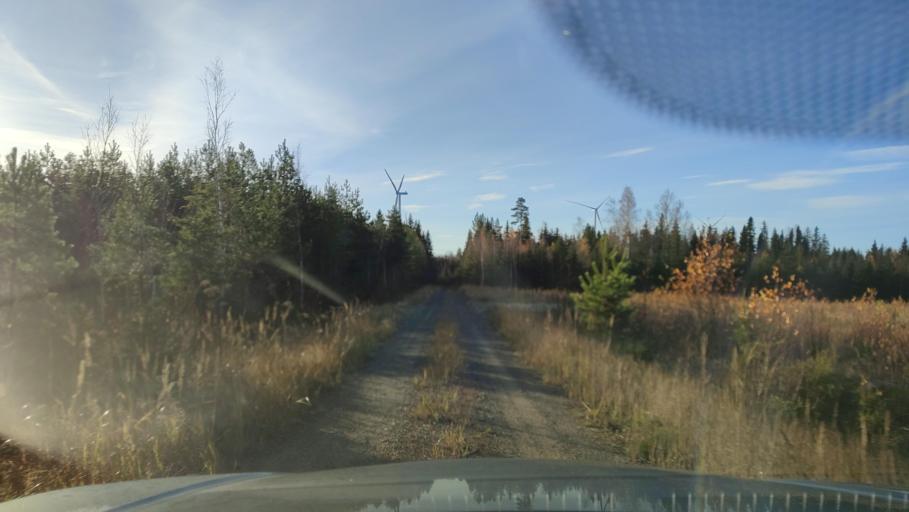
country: FI
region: Southern Ostrobothnia
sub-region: Suupohja
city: Karijoki
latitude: 62.1779
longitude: 21.6079
